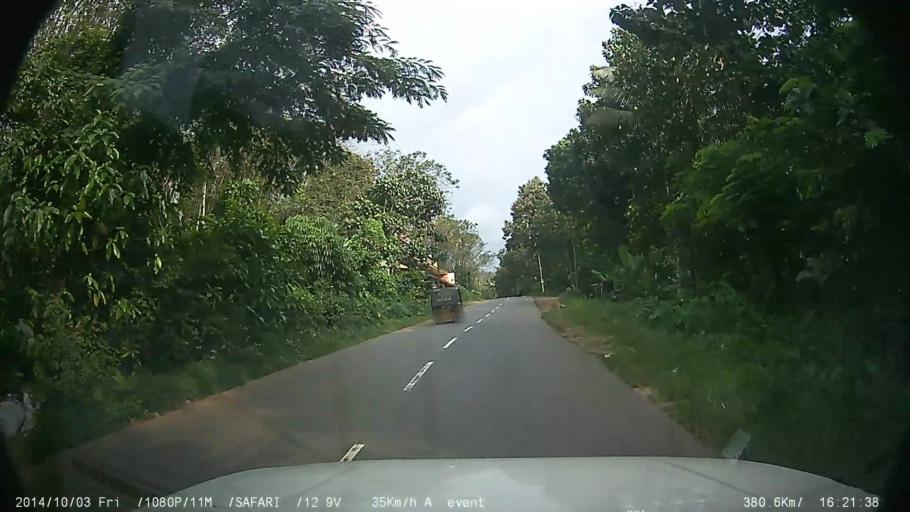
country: IN
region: Kerala
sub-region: Ernakulam
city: Piravam
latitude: 9.8836
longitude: 76.5925
